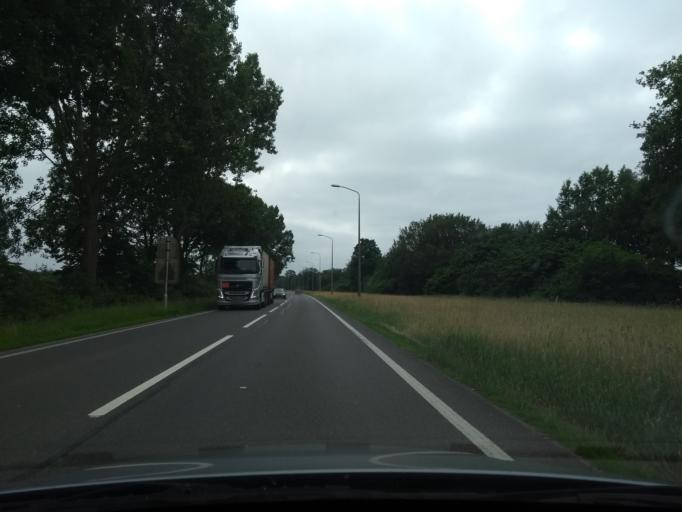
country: NL
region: Overijssel
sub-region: Gemeente Wierden
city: Wierden
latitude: 52.3488
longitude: 6.6247
